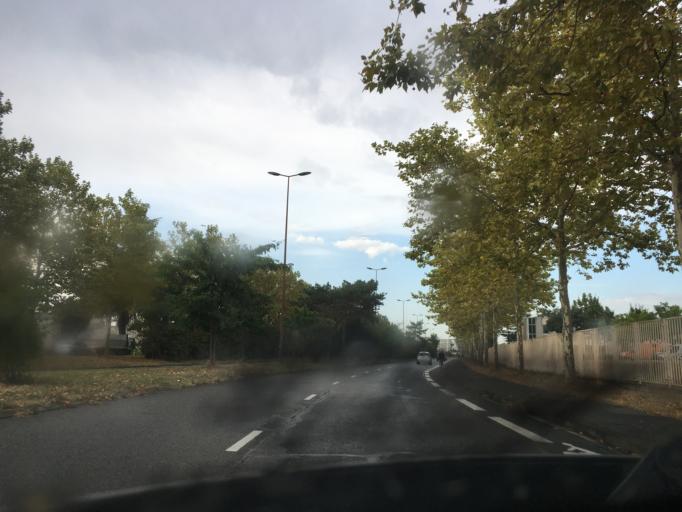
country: FR
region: Midi-Pyrenees
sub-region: Departement de la Haute-Garonne
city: Portet-sur-Garonne
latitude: 43.5654
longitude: 1.3933
